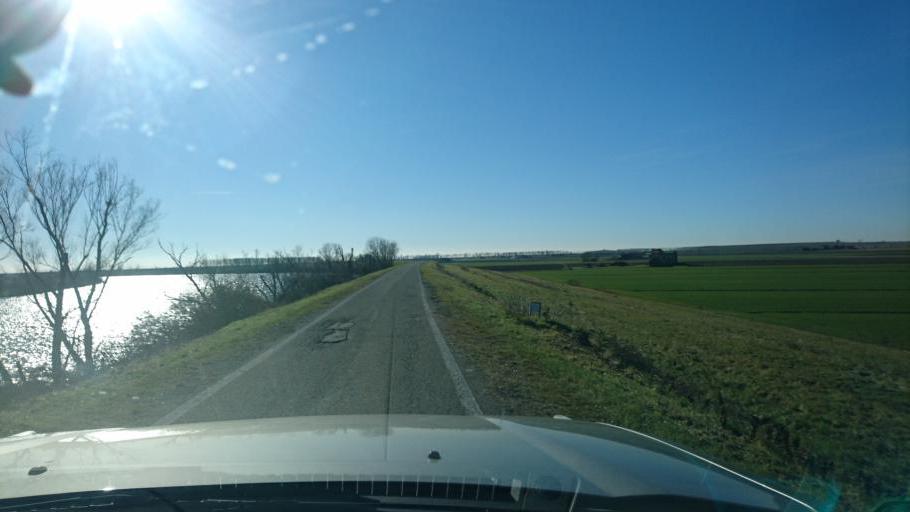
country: IT
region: Veneto
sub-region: Provincia di Rovigo
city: Ariano
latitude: 44.9398
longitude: 12.1625
